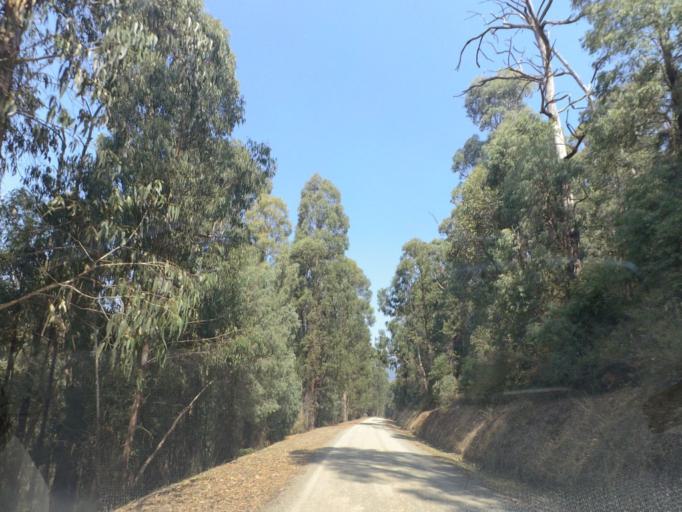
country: AU
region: Victoria
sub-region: Yarra Ranges
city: Millgrove
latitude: -37.5444
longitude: 145.7216
